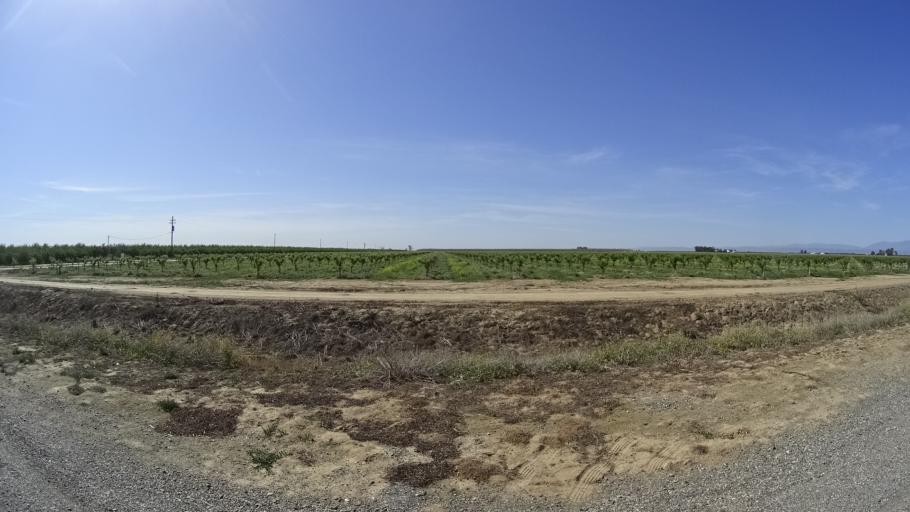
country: US
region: California
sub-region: Glenn County
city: Willows
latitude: 39.6238
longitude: -122.1386
